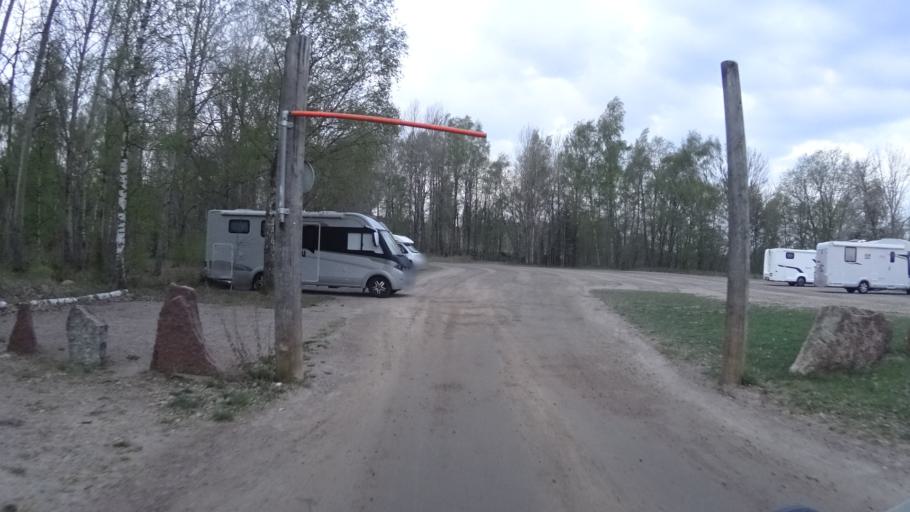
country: SE
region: Vaestra Goetaland
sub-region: Gotene Kommun
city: Goetene
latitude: 58.6188
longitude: 13.4025
